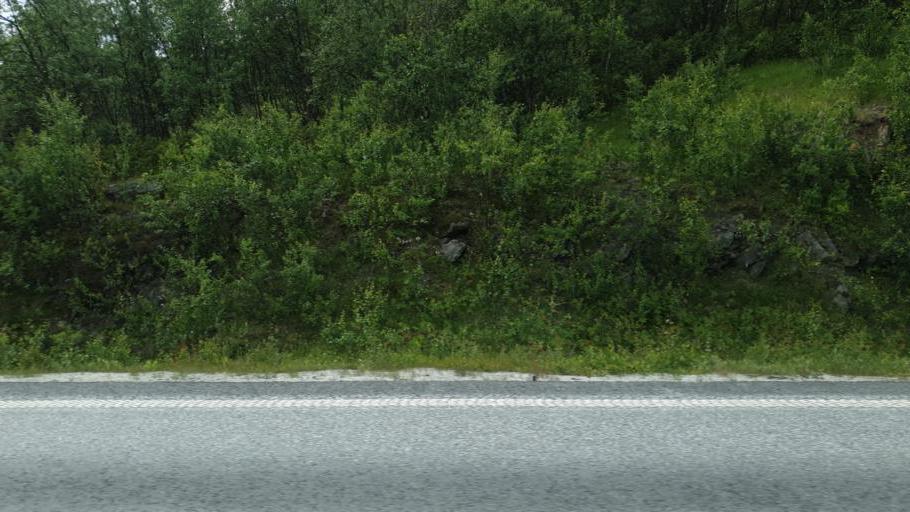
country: NO
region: Oppland
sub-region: Dovre
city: Dovre
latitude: 62.2104
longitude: 9.5596
